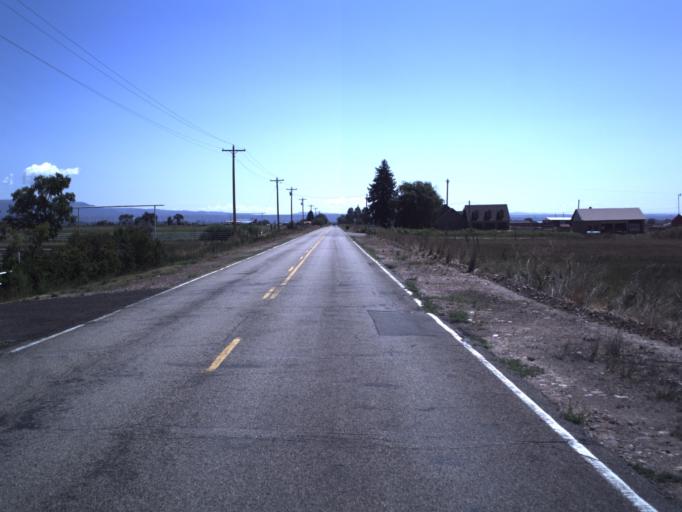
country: US
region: Utah
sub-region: Duchesne County
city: Roosevelt
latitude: 40.4329
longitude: -109.9940
